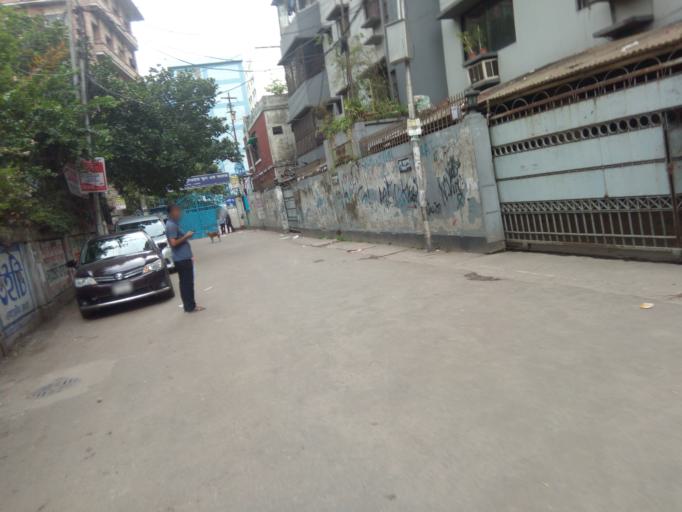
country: BD
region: Dhaka
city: Paltan
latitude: 23.7383
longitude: 90.4069
